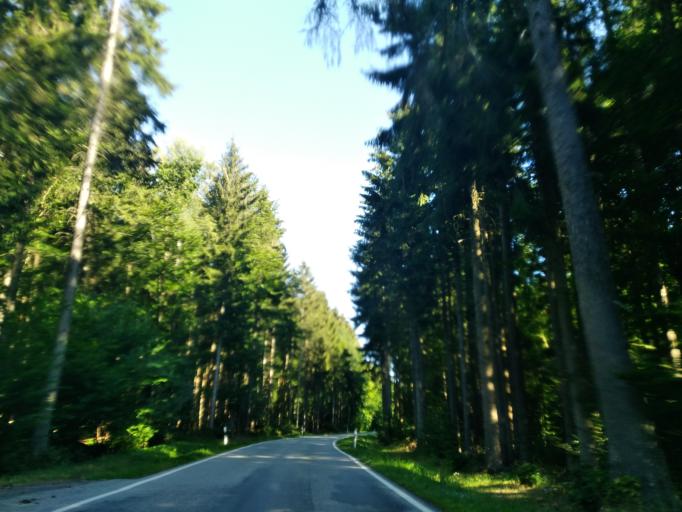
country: DE
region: Baden-Wuerttemberg
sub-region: Karlsruhe Region
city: Mudau
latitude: 49.5068
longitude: 9.2086
